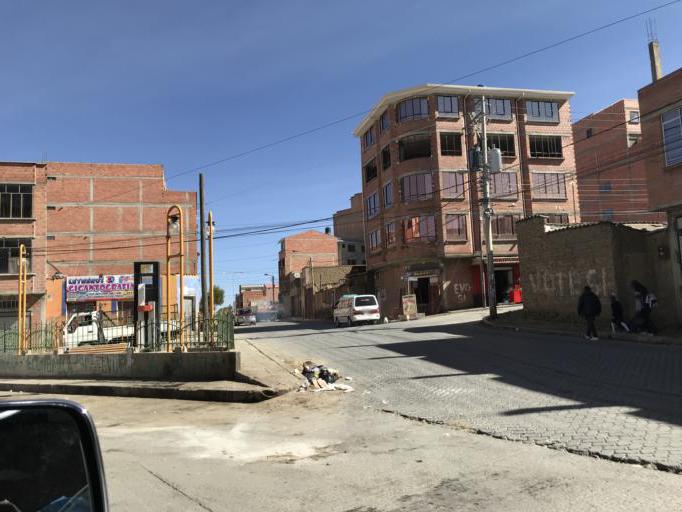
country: BO
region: La Paz
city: La Paz
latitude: -16.4867
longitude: -68.1769
